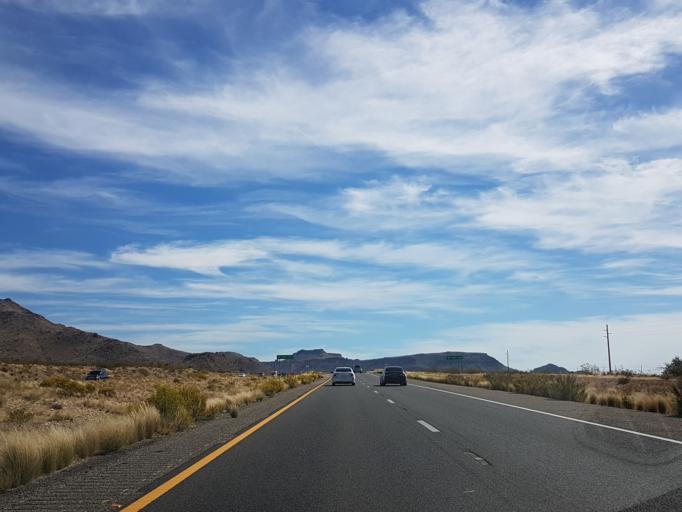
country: US
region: Arizona
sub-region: Mohave County
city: Golden Valley
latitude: 35.2539
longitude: -114.1560
